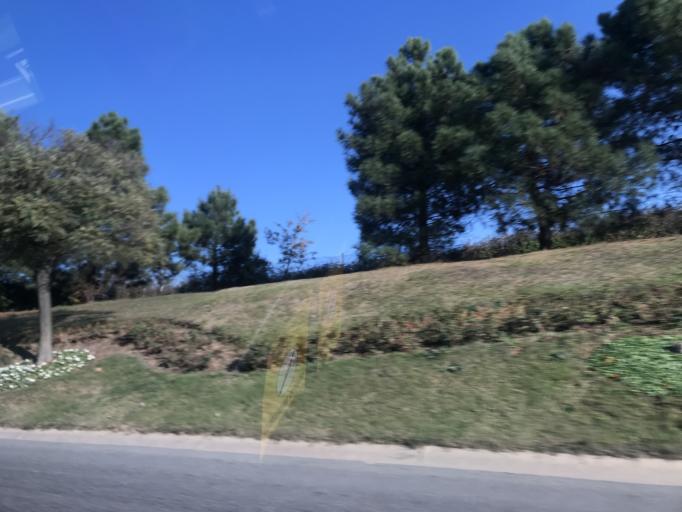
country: TR
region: Istanbul
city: Sultanbeyli
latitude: 40.9380
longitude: 29.3326
